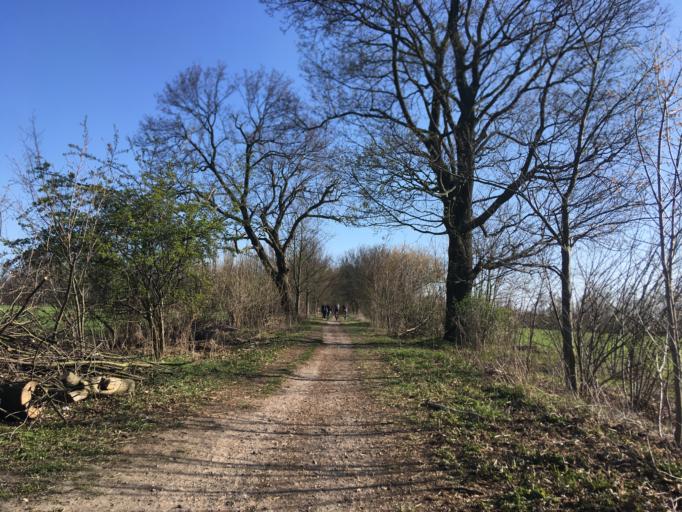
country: DE
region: Berlin
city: Stadtrandsiedlung Malchow
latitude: 52.5908
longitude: 13.4846
